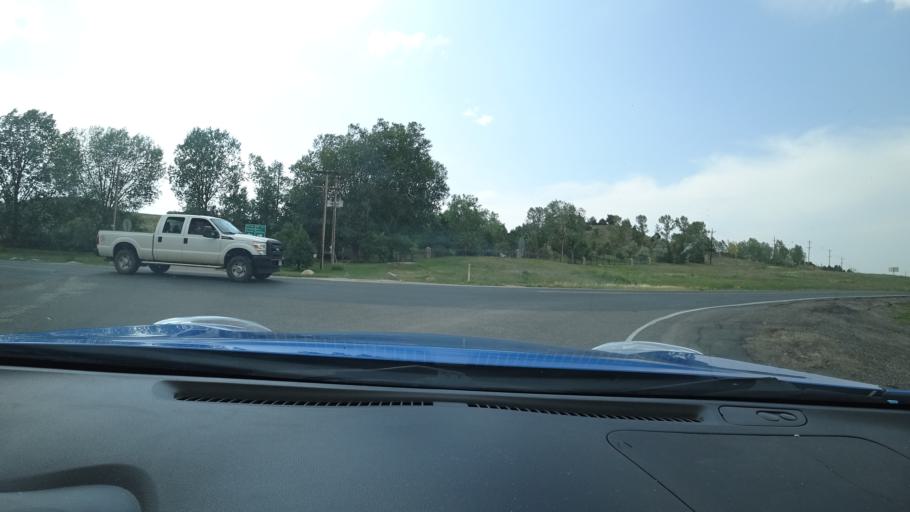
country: US
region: Colorado
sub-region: Adams County
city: Todd Creek
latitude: 39.9253
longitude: -104.8834
